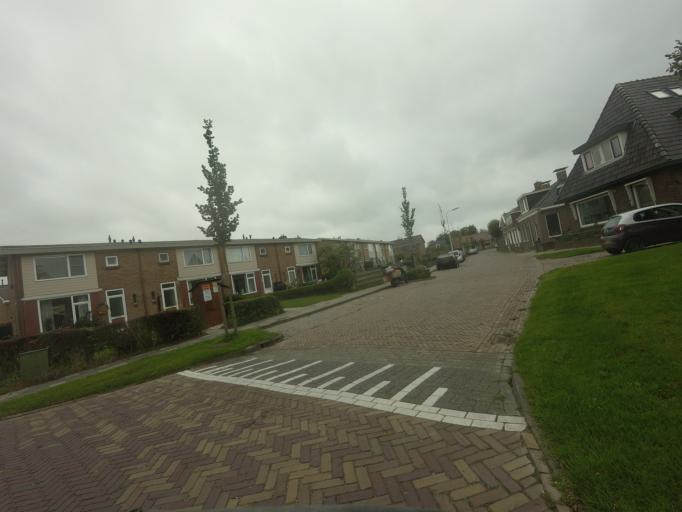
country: NL
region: Friesland
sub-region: Gemeente Ferwerderadiel
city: Ferwert
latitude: 53.3516
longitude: 5.8632
